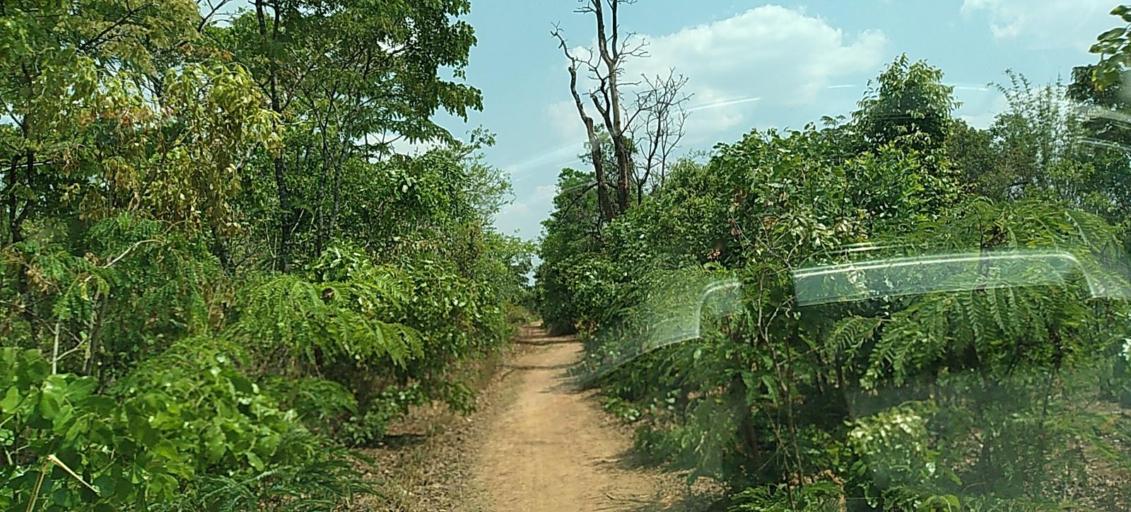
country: CD
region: Katanga
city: Kipushi
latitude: -12.0165
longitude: 27.4340
